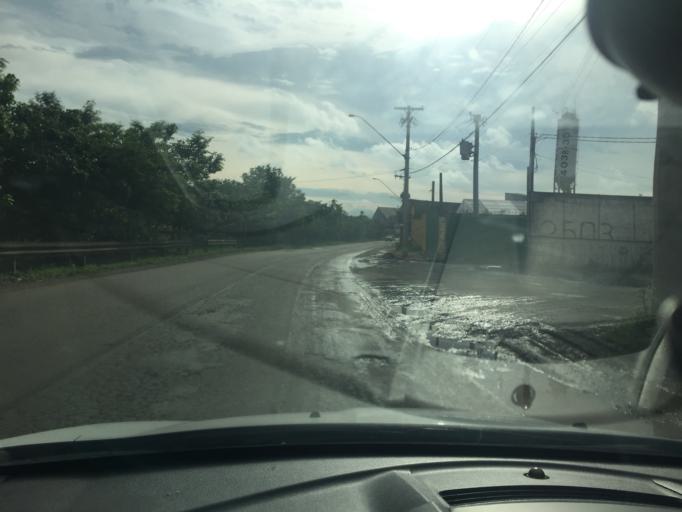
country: BR
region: Sao Paulo
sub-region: Campo Limpo Paulista
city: Campo Limpo Paulista
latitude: -23.2024
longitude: -46.8005
